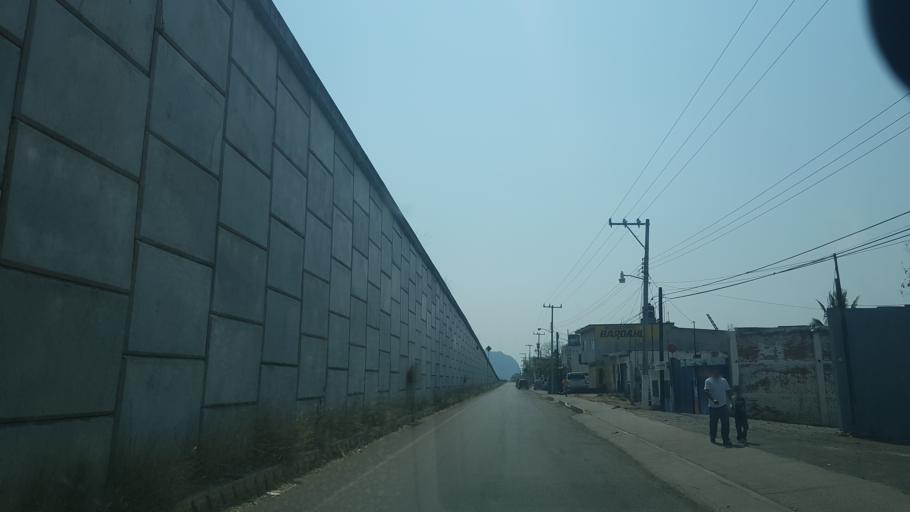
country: MX
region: Morelos
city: Amayuca
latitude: 18.7173
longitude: -98.7946
